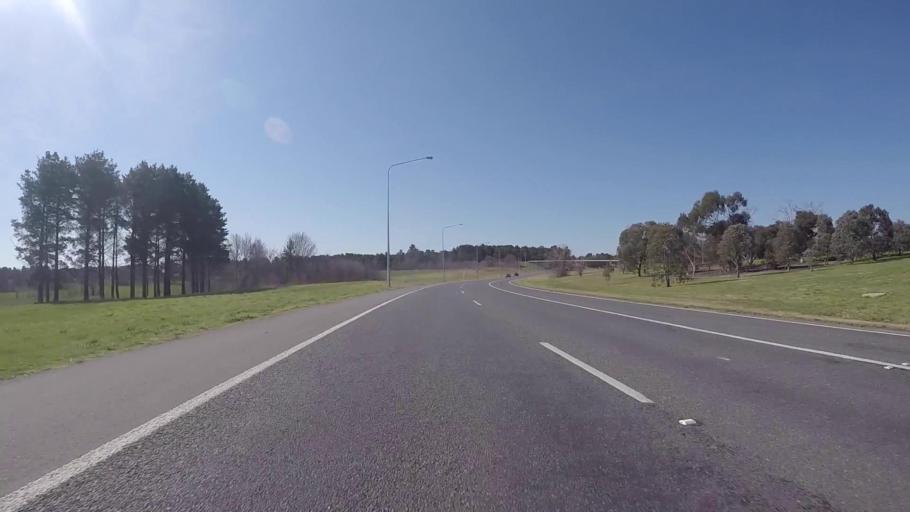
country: AU
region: Australian Capital Territory
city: Forrest
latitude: -35.3170
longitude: 149.0900
